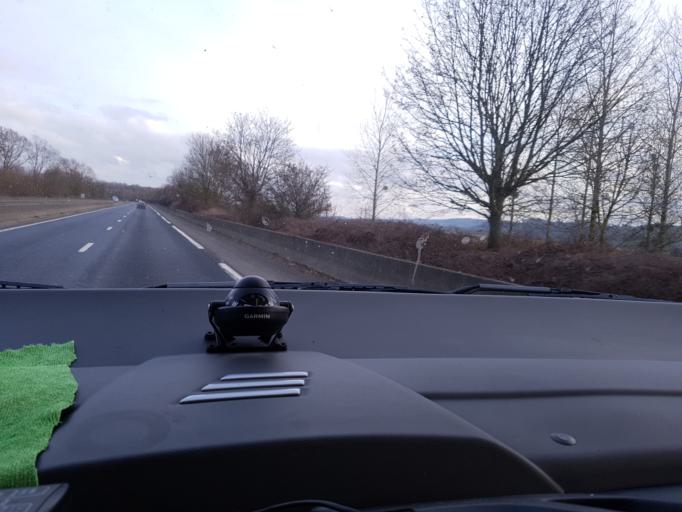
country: FR
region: Champagne-Ardenne
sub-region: Departement des Ardennes
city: Balan
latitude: 49.6852
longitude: 4.9554
